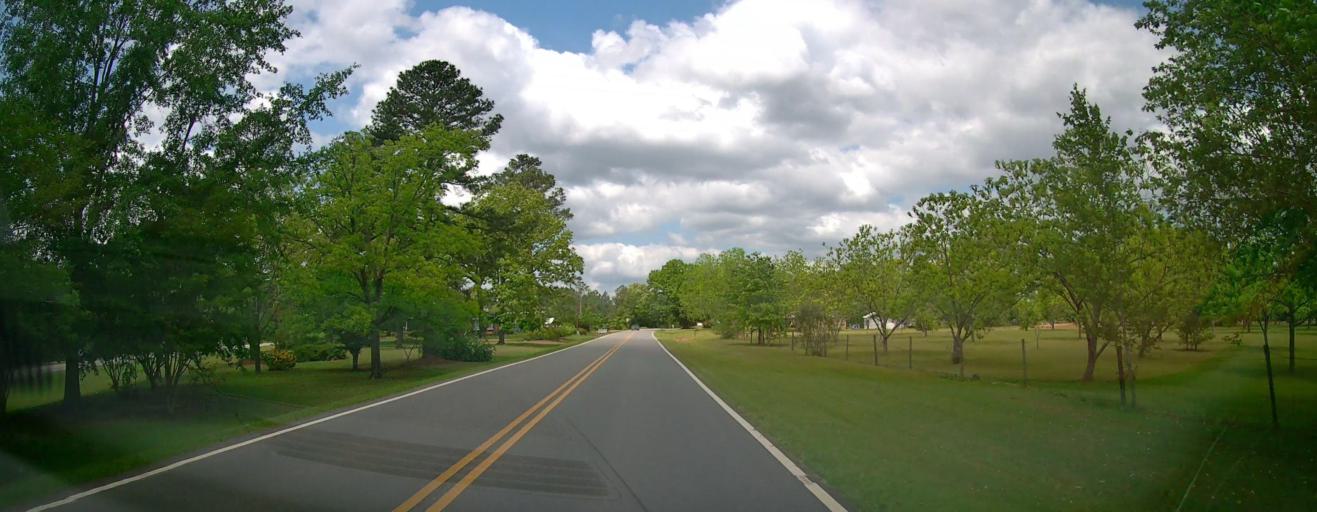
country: US
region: Georgia
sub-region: Laurens County
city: Dublin
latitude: 32.5892
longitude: -82.9461
